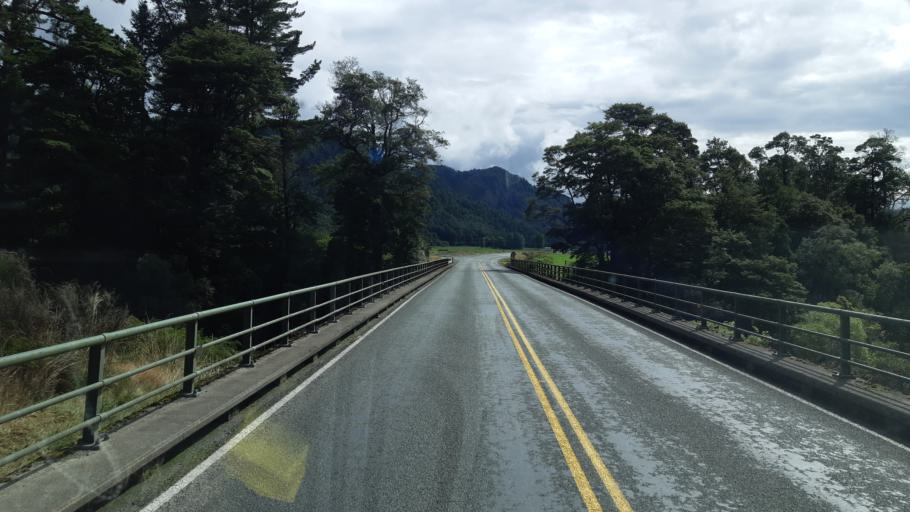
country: NZ
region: Tasman
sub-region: Tasman District
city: Wakefield
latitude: -41.7745
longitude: 172.3784
